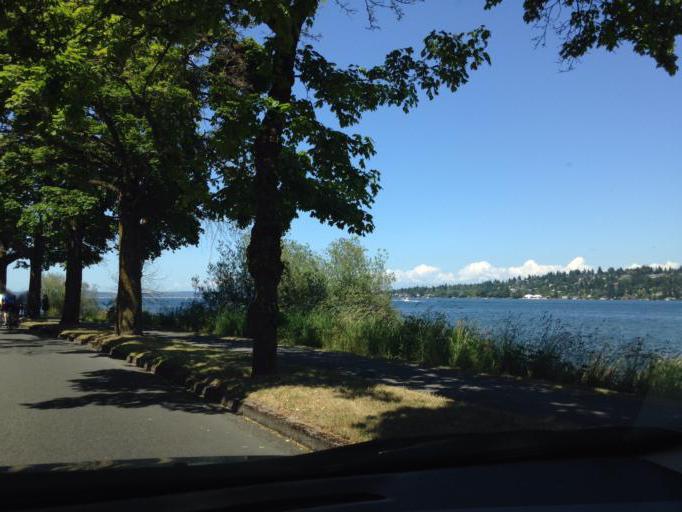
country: US
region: Washington
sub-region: King County
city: Mercer Island
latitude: 47.5655
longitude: -122.2680
